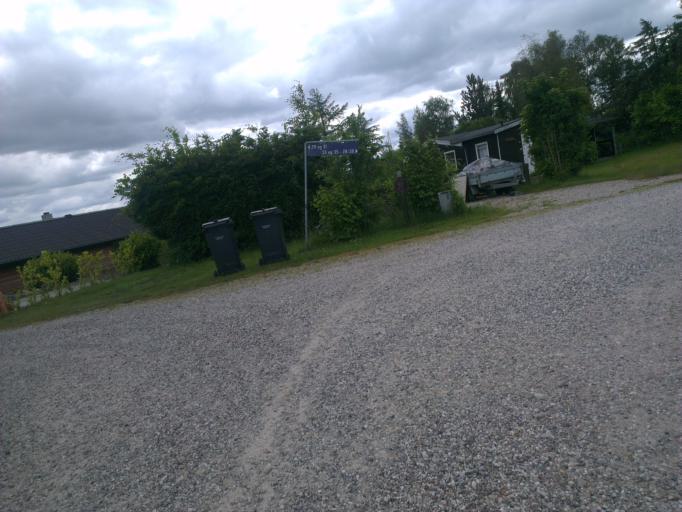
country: DK
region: Capital Region
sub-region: Frederikssund Kommune
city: Frederikssund
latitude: 55.8075
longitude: 12.0396
